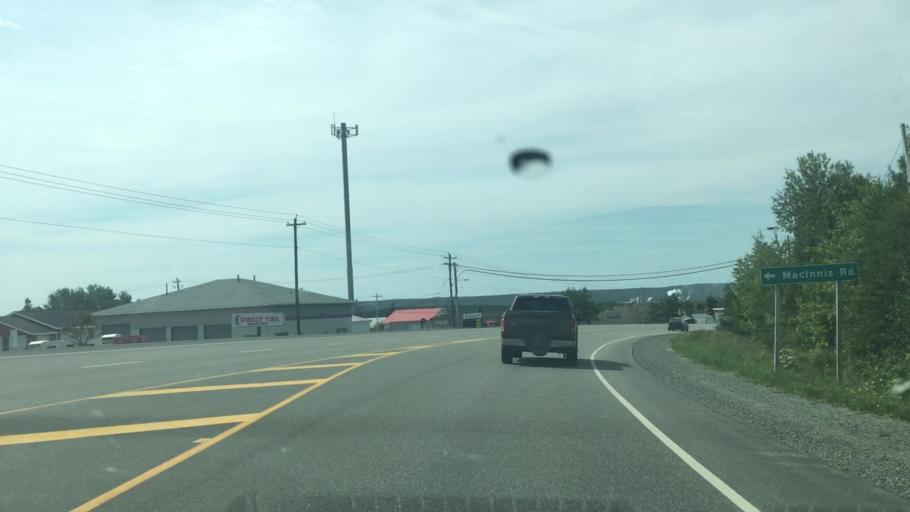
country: CA
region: Nova Scotia
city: Port Hawkesbury
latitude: 45.6168
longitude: -61.3362
